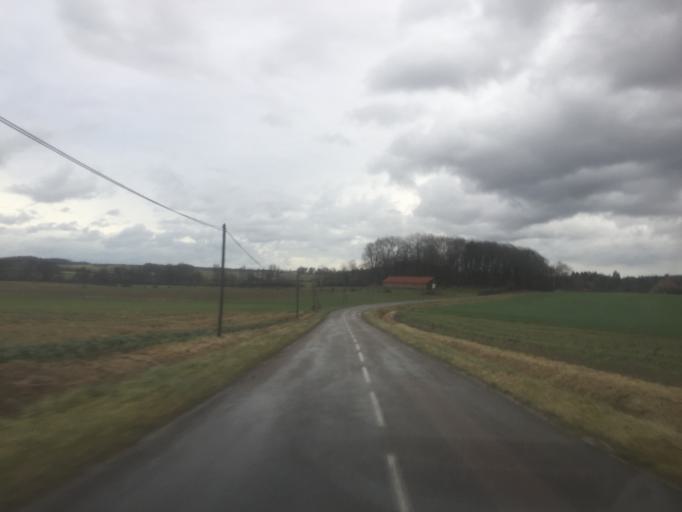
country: FR
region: Franche-Comte
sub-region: Departement de la Haute-Saone
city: Pesmes
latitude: 47.2189
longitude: 5.5080
